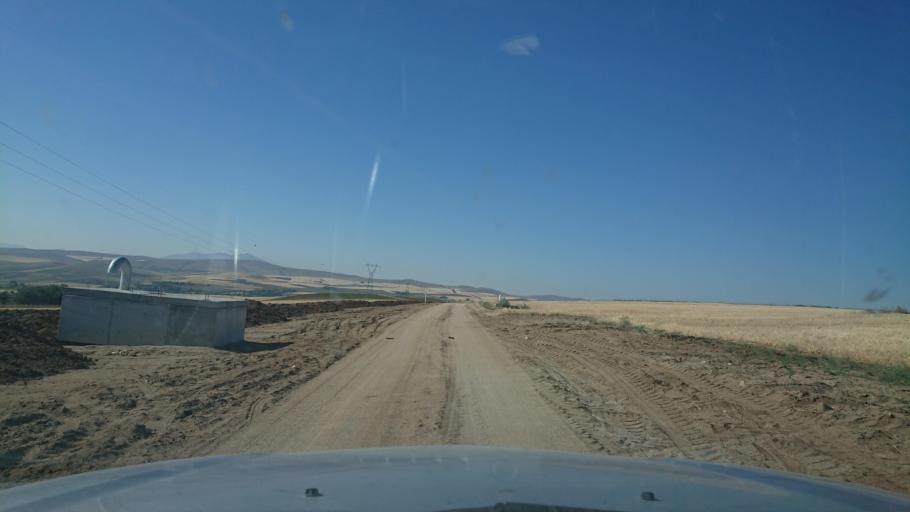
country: TR
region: Aksaray
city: Agacoren
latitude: 38.8414
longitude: 33.9442
